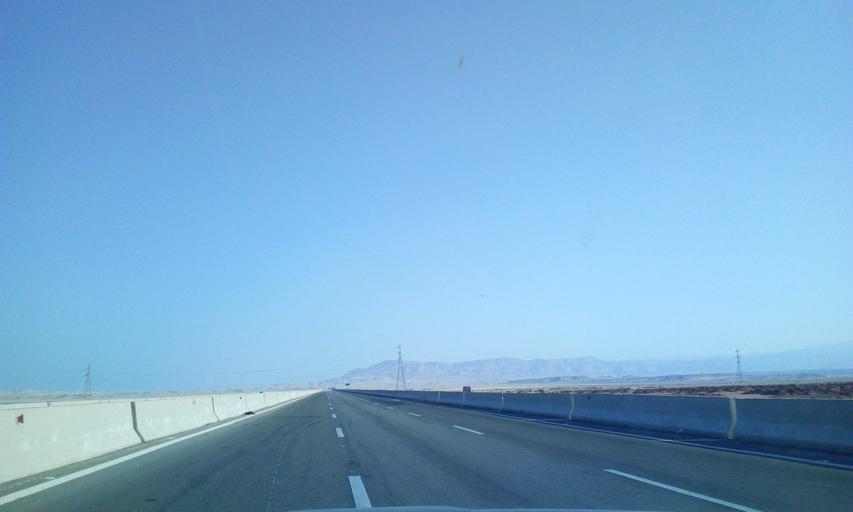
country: EG
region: As Suways
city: Ain Sukhna
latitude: 29.1253
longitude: 32.5263
